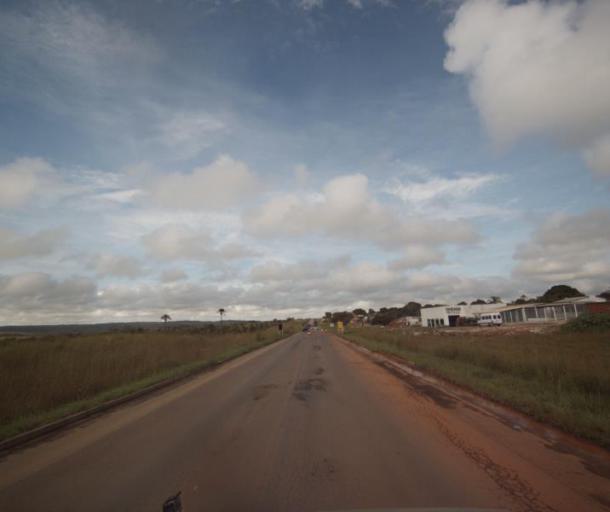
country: BR
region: Goias
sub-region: Pirenopolis
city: Pirenopolis
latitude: -15.7706
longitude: -48.7615
